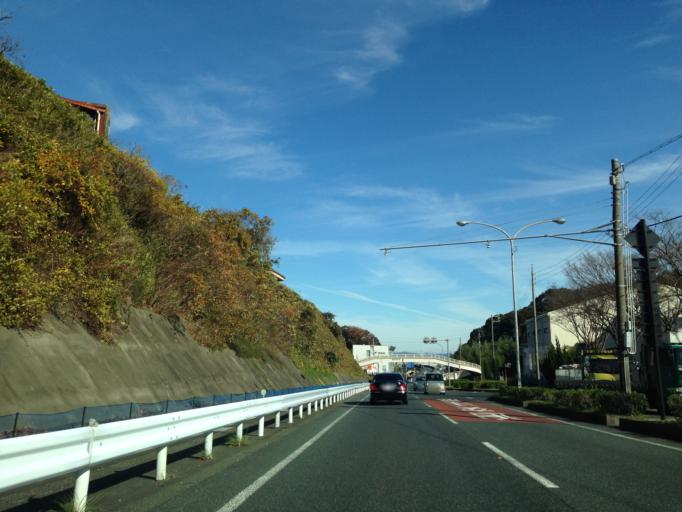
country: JP
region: Shizuoka
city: Fukuroi
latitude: 34.7353
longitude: 137.8796
